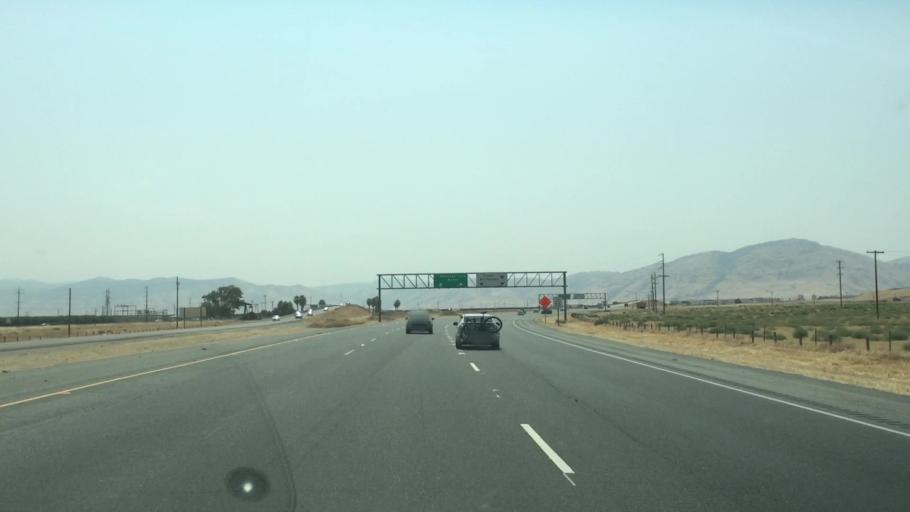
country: US
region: California
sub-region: Kern County
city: Frazier Park
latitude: 35.0226
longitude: -118.9609
